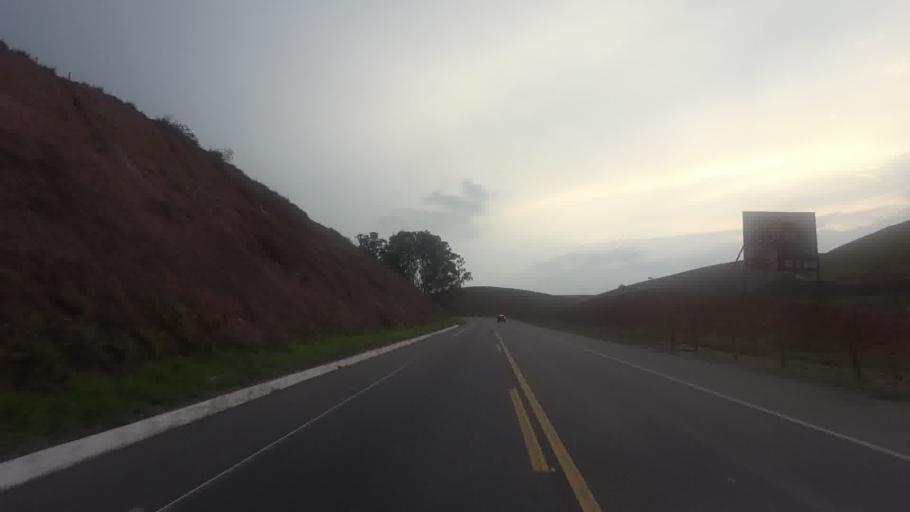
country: BR
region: Rio de Janeiro
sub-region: Carmo
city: Carmo
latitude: -21.8005
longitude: -42.5713
